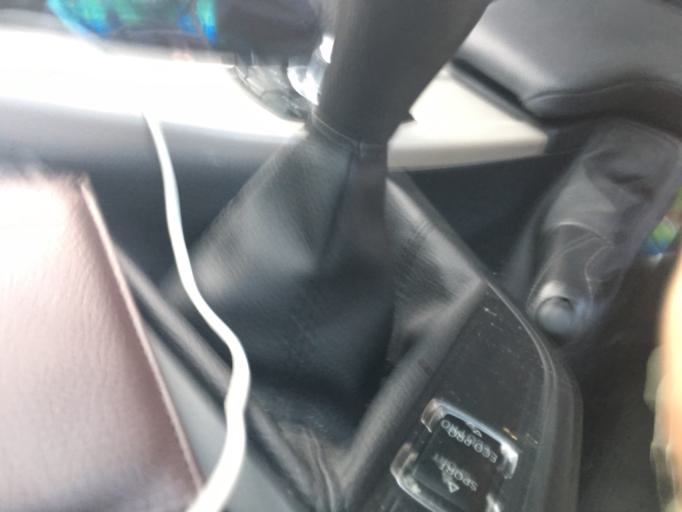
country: HR
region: Grad Zagreb
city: Novi Zagreb
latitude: 45.7780
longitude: 15.9657
